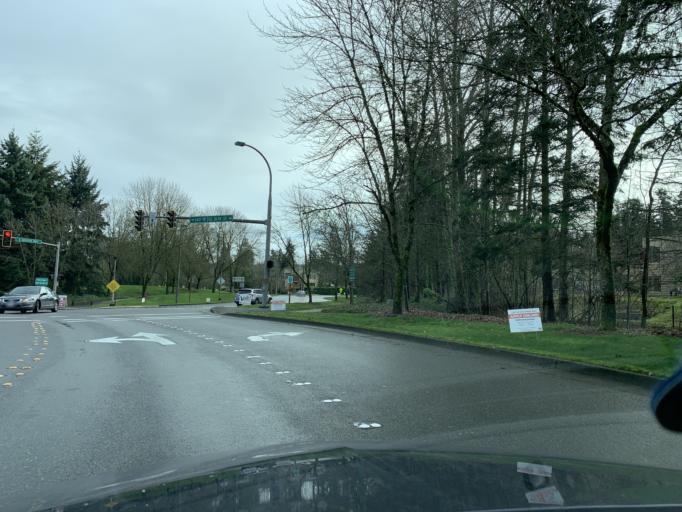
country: US
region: Washington
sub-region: King County
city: Mercer Island
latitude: 47.5773
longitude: -122.2078
